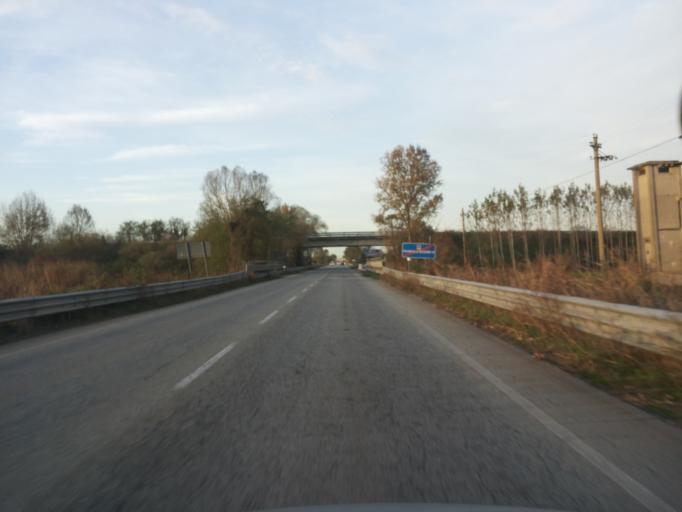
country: IT
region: Piedmont
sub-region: Provincia di Alessandria
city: Pontestura
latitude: 45.1692
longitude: 8.3322
